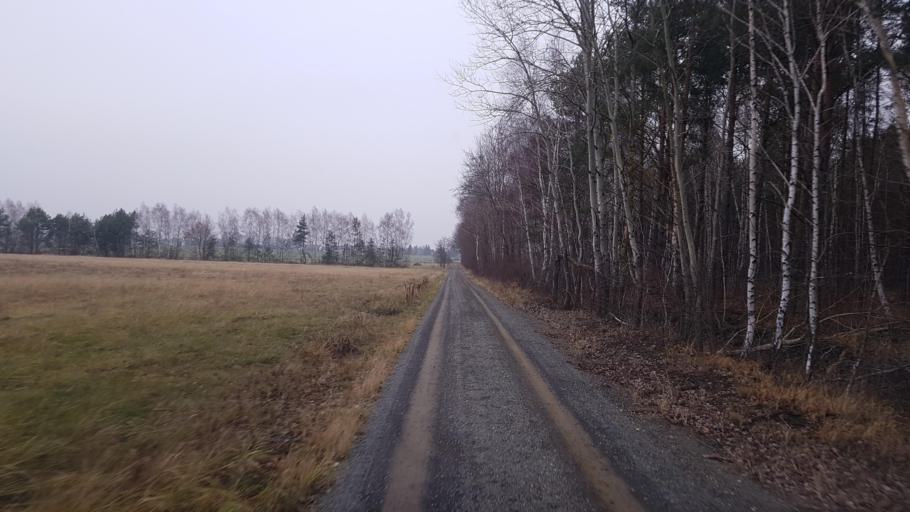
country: DE
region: Brandenburg
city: Plessa
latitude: 51.5251
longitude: 13.6276
